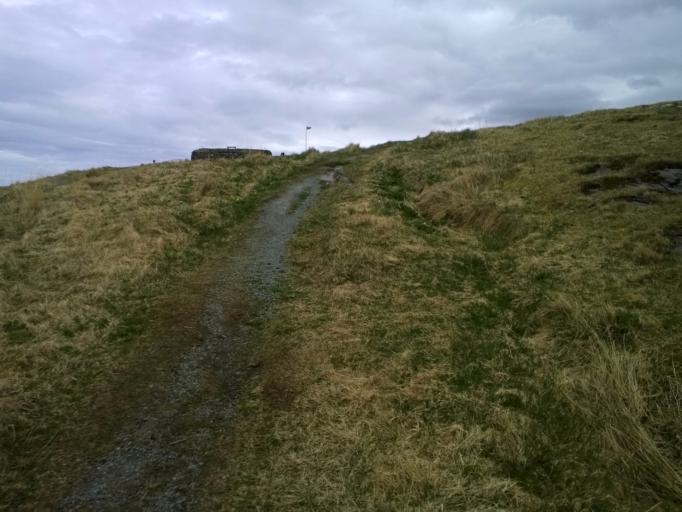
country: NO
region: Nordland
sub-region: Bodo
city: Bodo
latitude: 67.2866
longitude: 14.3653
